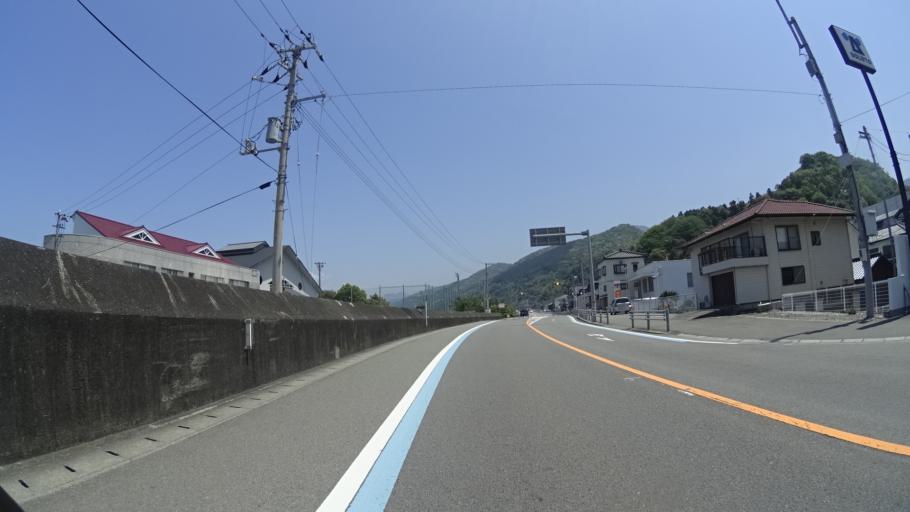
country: JP
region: Ehime
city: Ozu
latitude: 33.6517
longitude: 132.5789
